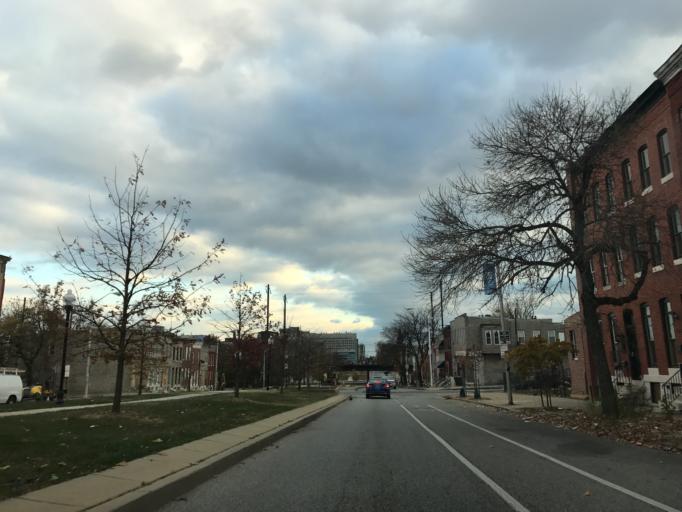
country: US
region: Maryland
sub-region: City of Baltimore
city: Baltimore
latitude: 39.3080
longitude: -76.5950
